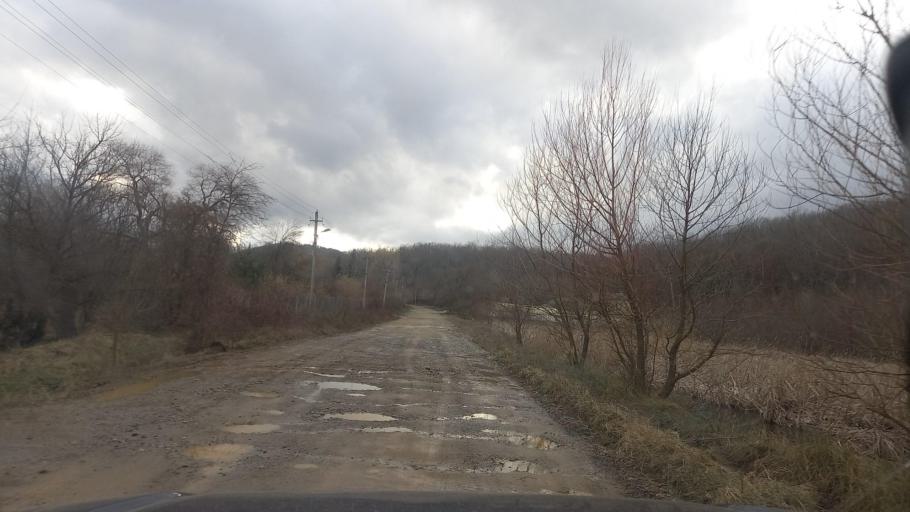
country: RU
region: Krasnodarskiy
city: Smolenskaya
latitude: 44.5649
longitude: 38.8022
